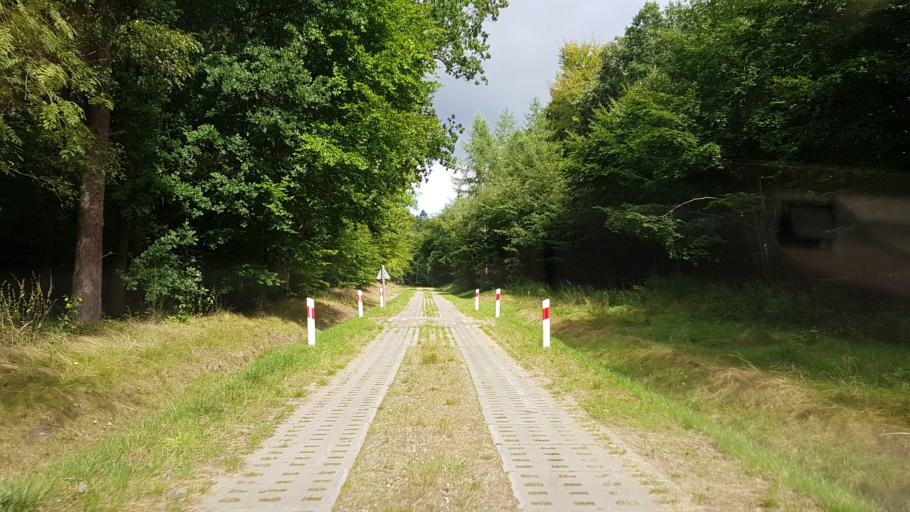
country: PL
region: West Pomeranian Voivodeship
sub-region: Powiat bialogardzki
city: Tychowo
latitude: 53.9776
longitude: 16.3855
